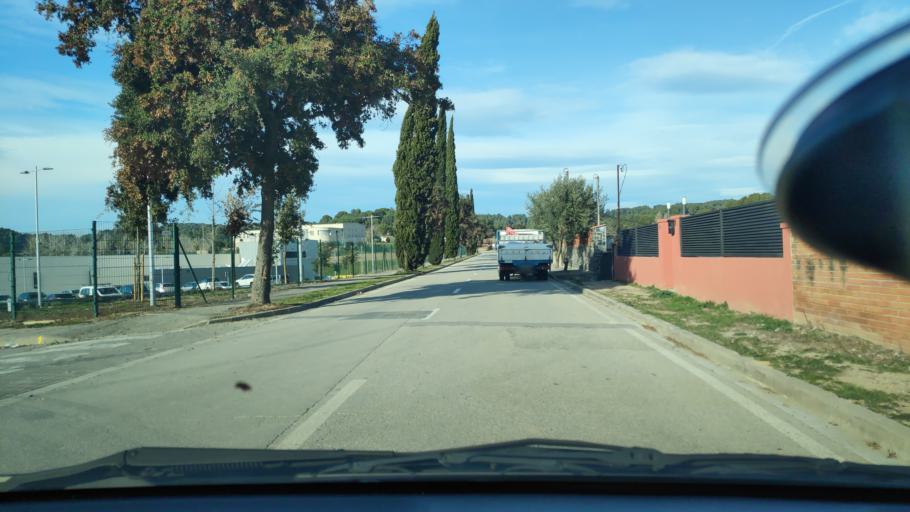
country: ES
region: Catalonia
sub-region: Provincia de Barcelona
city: Rubi
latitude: 41.4942
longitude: 2.0653
